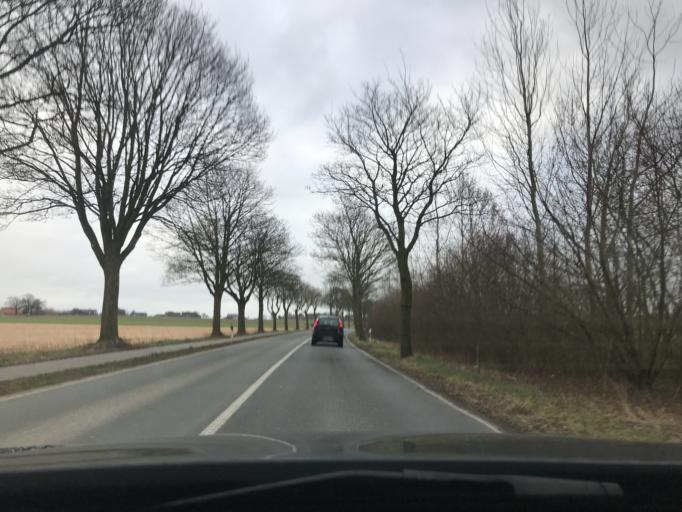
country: DE
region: North Rhine-Westphalia
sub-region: Regierungsbezirk Dusseldorf
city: Kleve
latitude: 51.7484
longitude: 6.1917
